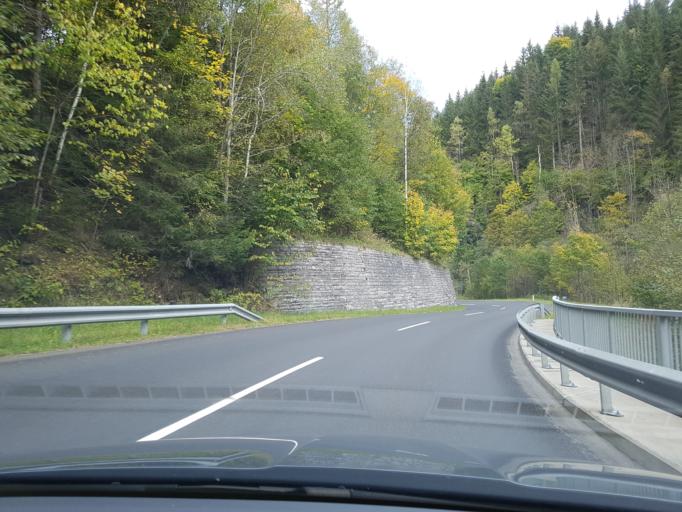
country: AT
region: Styria
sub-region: Politischer Bezirk Murau
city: Stadl an der Mur
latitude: 47.0586
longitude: 13.9134
